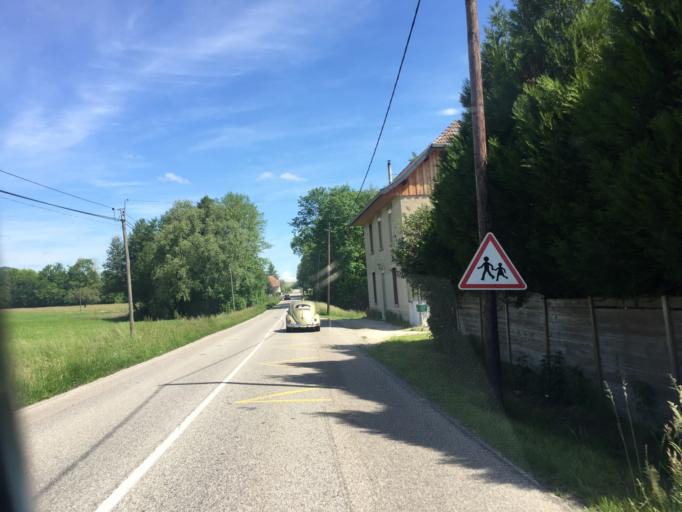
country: FR
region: Rhone-Alpes
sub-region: Departement de la Savoie
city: Albens
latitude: 45.8005
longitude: 5.9492
